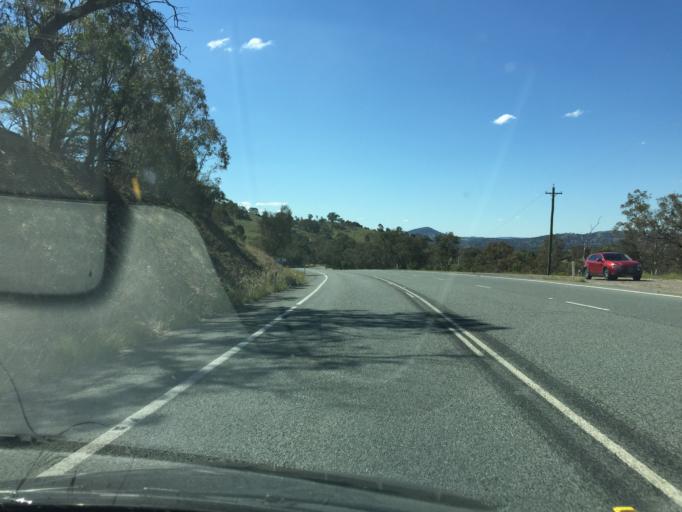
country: AU
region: Australian Capital Territory
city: Macarthur
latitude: -35.4587
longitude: 149.1322
